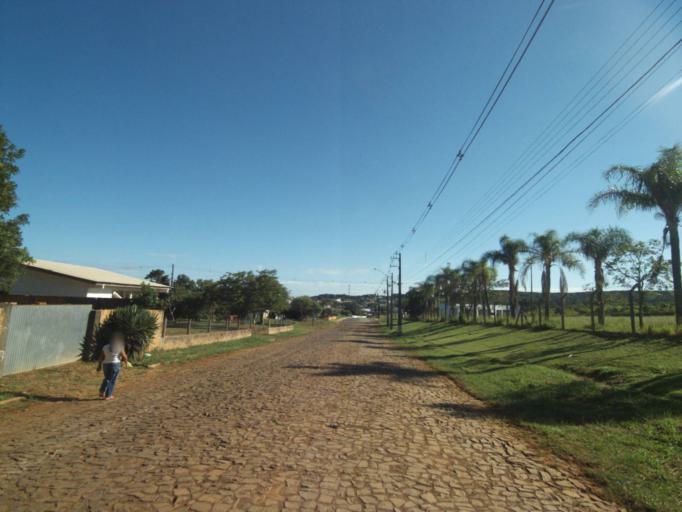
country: BR
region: Parana
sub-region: Pinhao
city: Pinhao
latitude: -25.8444
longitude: -52.0313
